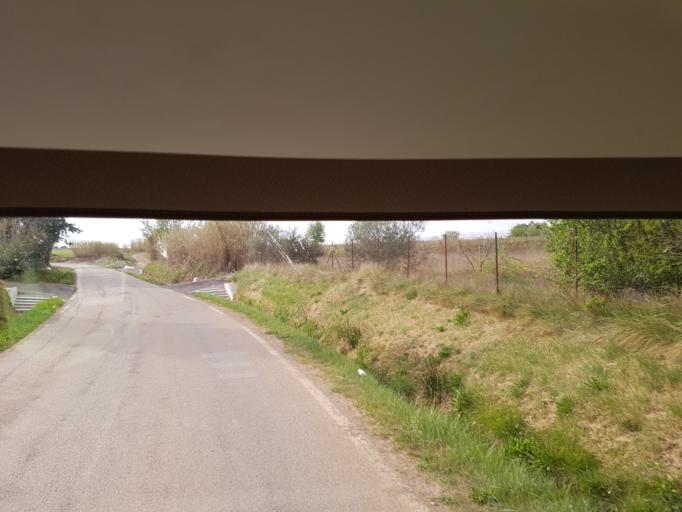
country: FR
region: Languedoc-Roussillon
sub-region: Departement de l'Herault
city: Marseillan
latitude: 43.3643
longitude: 3.5193
